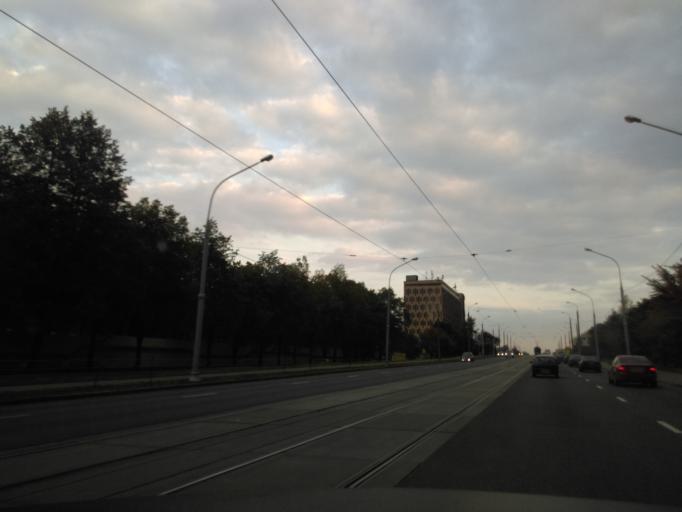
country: BY
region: Minsk
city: Minsk
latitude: 53.8959
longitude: 27.6076
